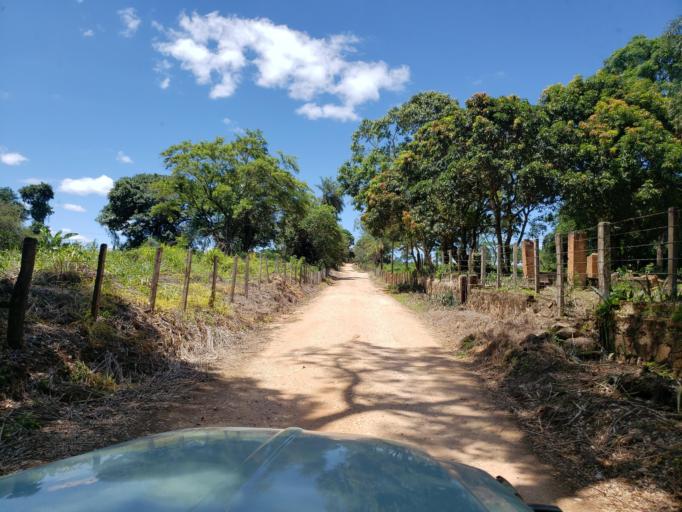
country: BR
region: Sao Paulo
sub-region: Moji-Guacu
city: Mogi-Gaucu
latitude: -22.3147
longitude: -46.8795
